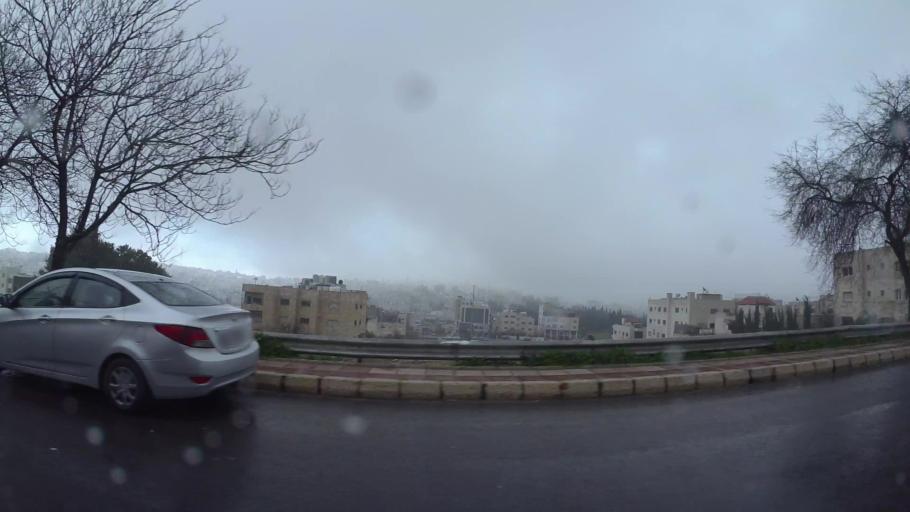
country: JO
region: Amman
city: Al Jubayhah
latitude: 32.0182
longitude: 35.8413
